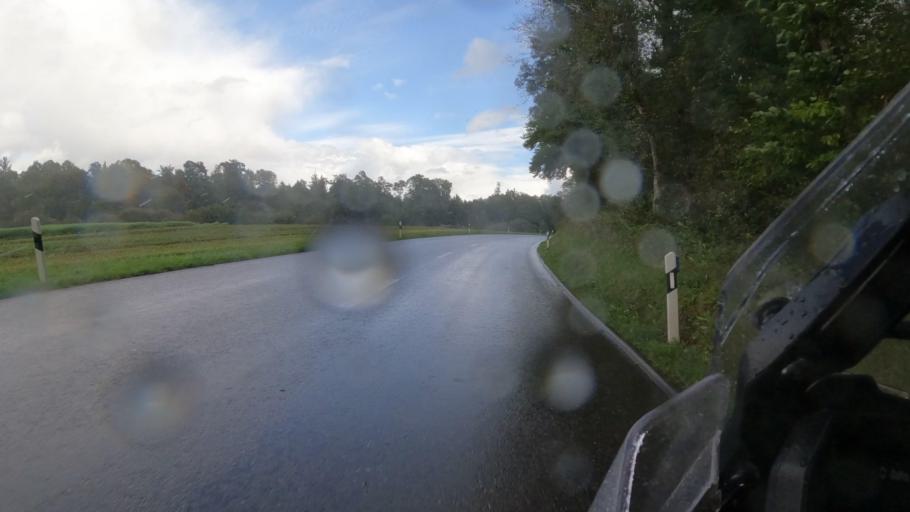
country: CH
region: Zurich
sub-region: Bezirk Andelfingen
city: Marthalen
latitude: 47.6407
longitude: 8.6379
